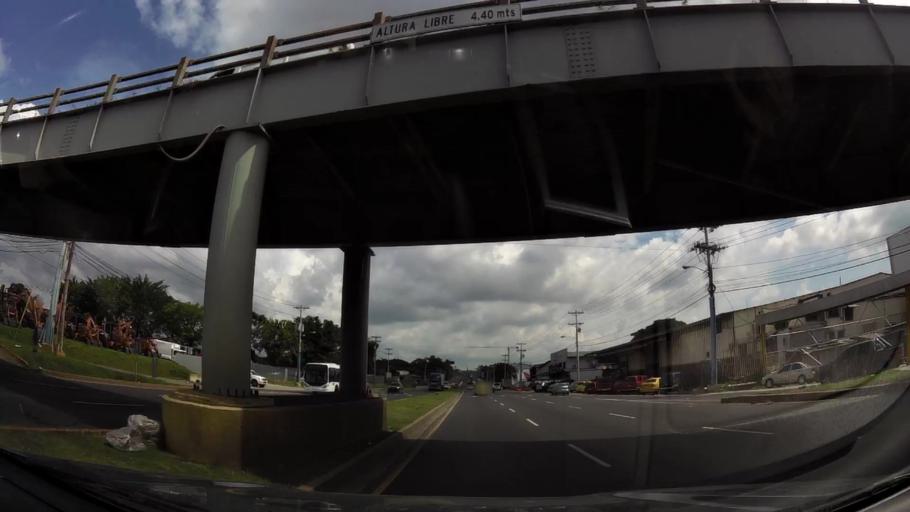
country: PA
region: Panama
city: San Miguelito
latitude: 9.0535
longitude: -79.4411
